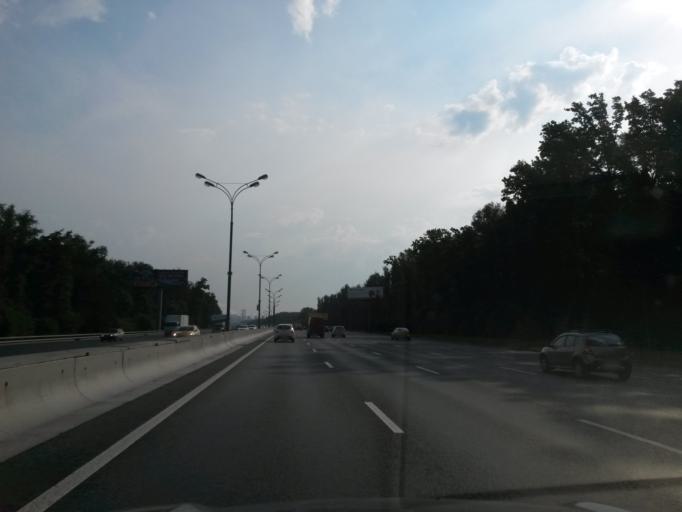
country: RU
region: Moskovskaya
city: Razvilka
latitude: 55.5999
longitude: 37.7488
